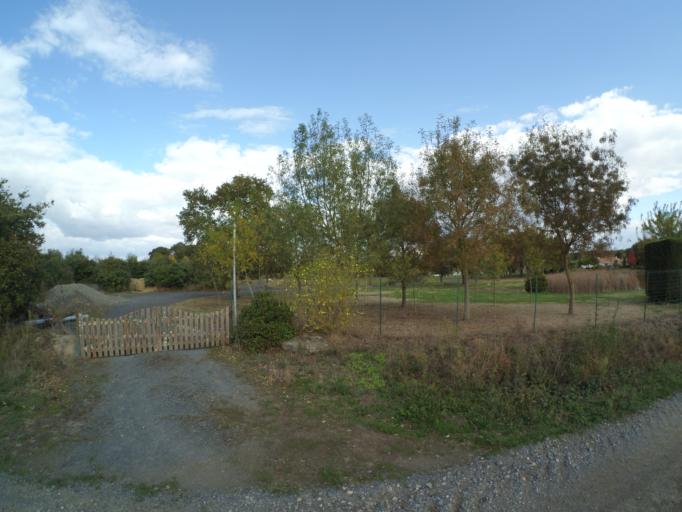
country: FR
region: Pays de la Loire
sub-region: Departement de la Loire-Atlantique
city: Saint-Lumine-de-Clisson
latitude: 47.0830
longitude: -1.3505
